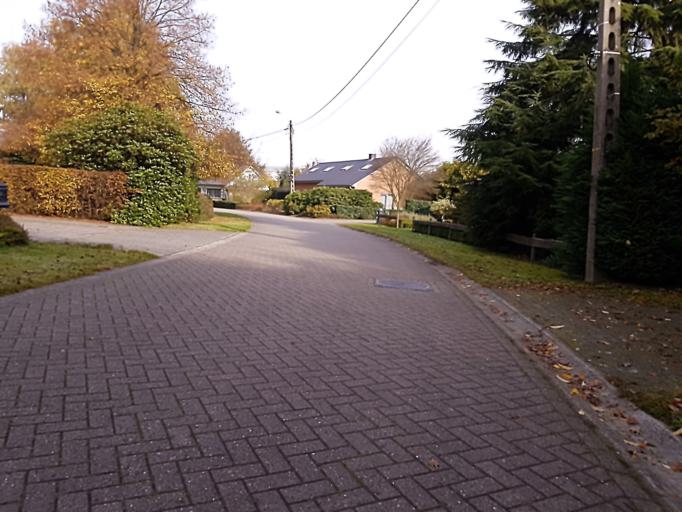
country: BE
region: Flanders
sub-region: Provincie Antwerpen
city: Sint-Katelijne-Waver
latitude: 51.0590
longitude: 4.5174
